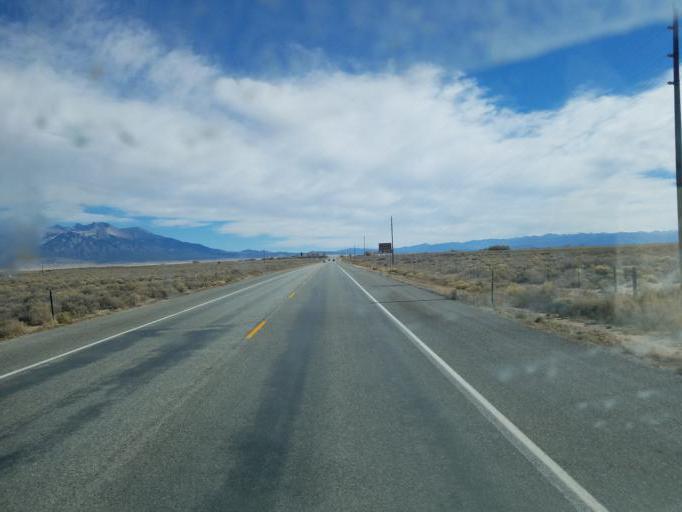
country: US
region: Colorado
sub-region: Alamosa County
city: Alamosa East
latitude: 37.4741
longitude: -105.7512
